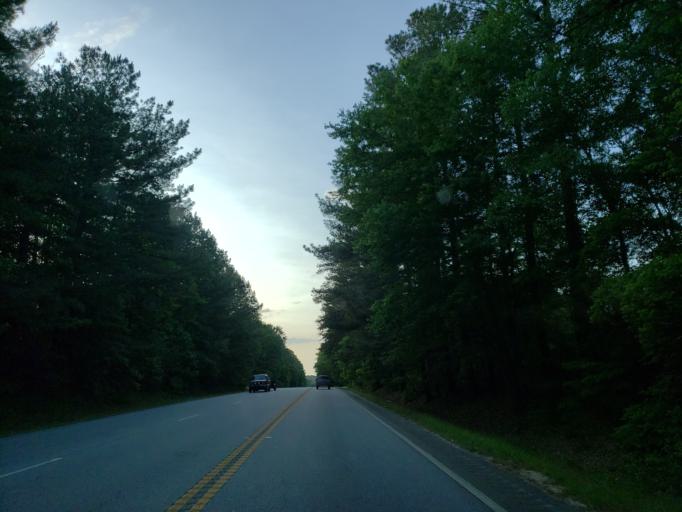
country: US
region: Georgia
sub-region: Coweta County
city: Newnan
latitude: 33.4663
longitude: -84.8944
